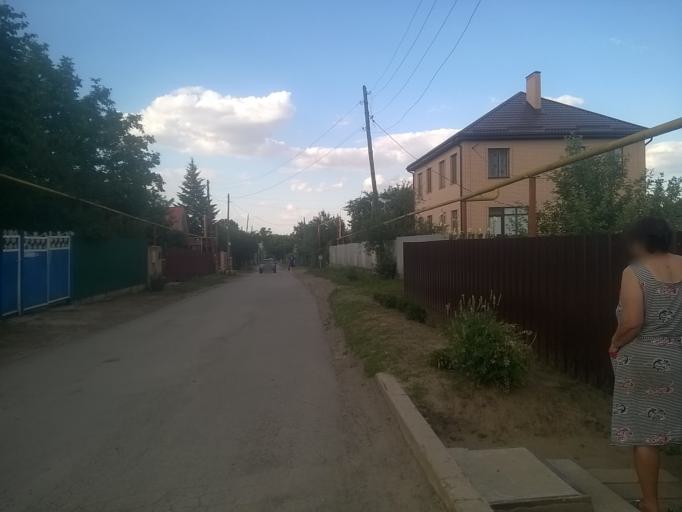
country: RU
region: Rostov
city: Donetsk
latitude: 48.3380
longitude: 39.9563
